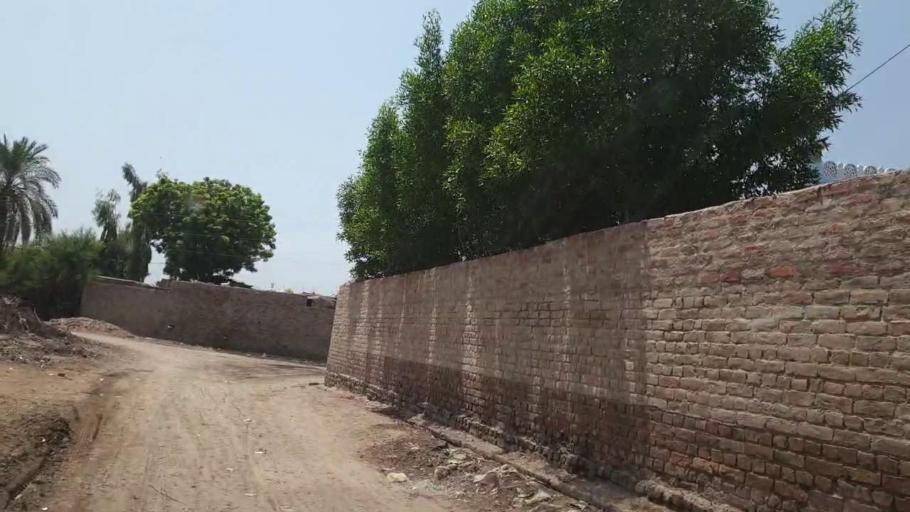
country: PK
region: Sindh
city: Lakhi
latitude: 27.8614
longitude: 68.6031
